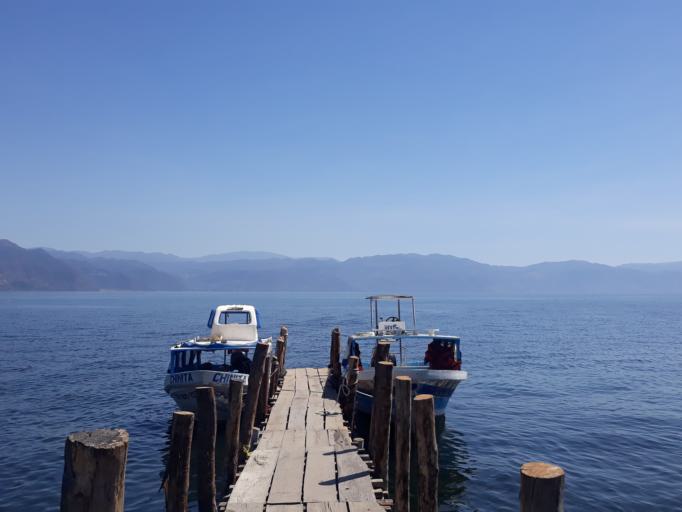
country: GT
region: Solola
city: San Pedro La Laguna
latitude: 14.6925
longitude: -91.2671
